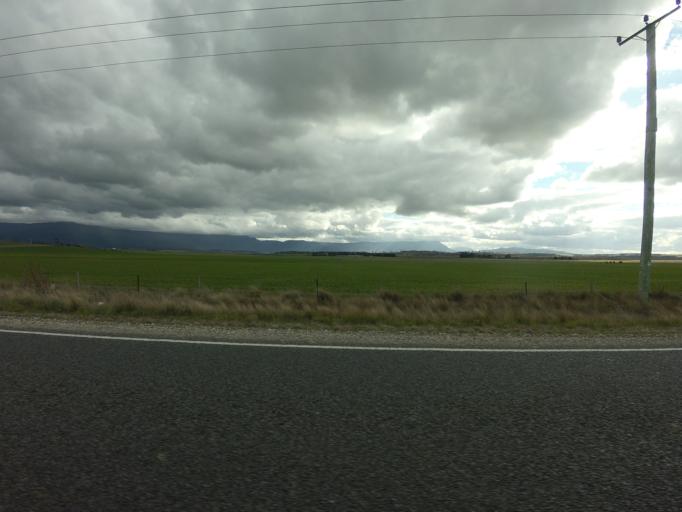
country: AU
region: Tasmania
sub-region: Northern Midlands
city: Longford
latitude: -41.7524
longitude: 147.0824
